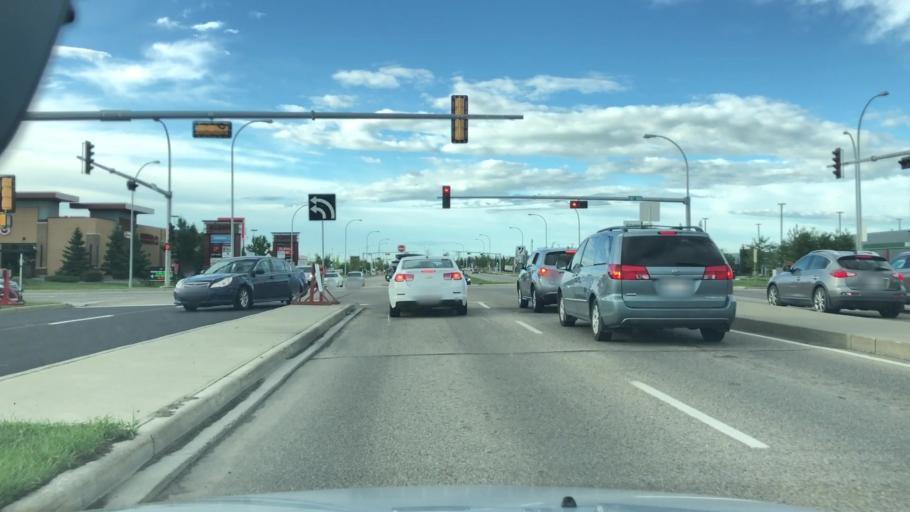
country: CA
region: Alberta
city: St. Albert
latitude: 53.6283
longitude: -113.5412
